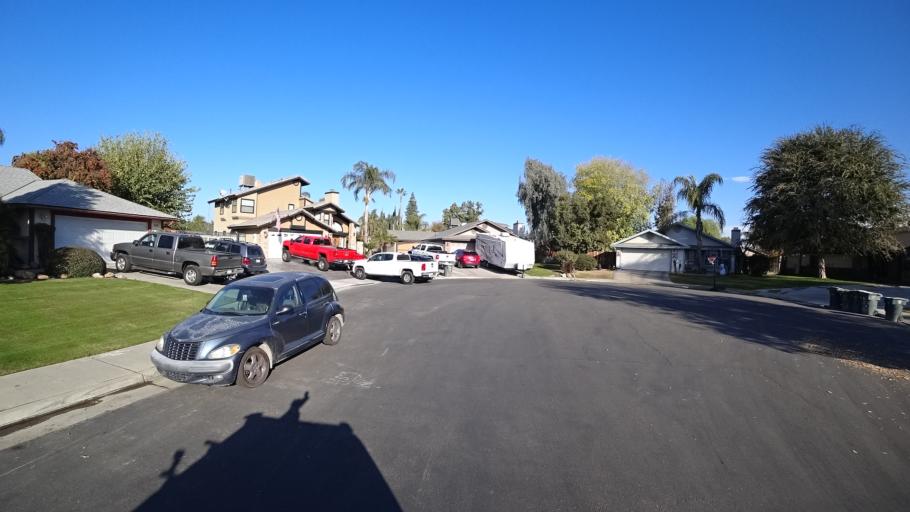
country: US
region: California
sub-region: Kern County
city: Rosedale
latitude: 35.3527
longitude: -119.1495
